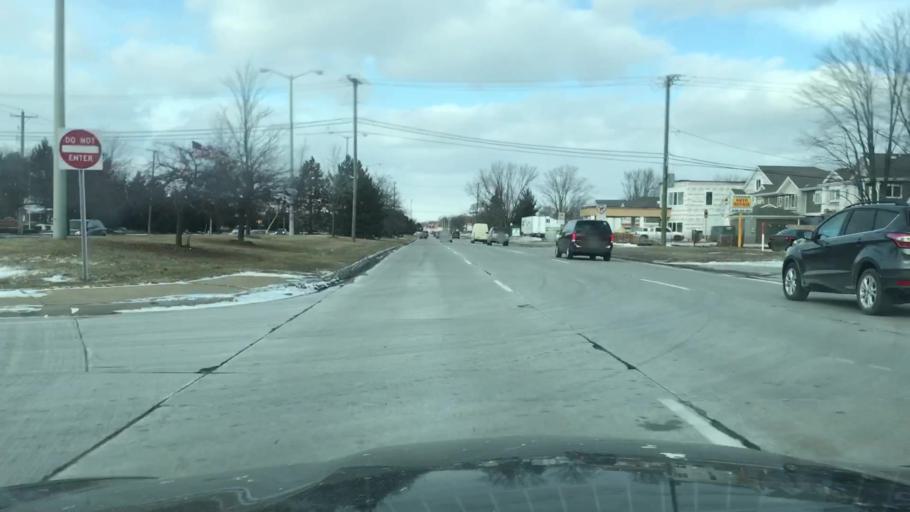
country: US
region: Michigan
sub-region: Macomb County
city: Utica
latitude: 42.6178
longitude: -83.0517
